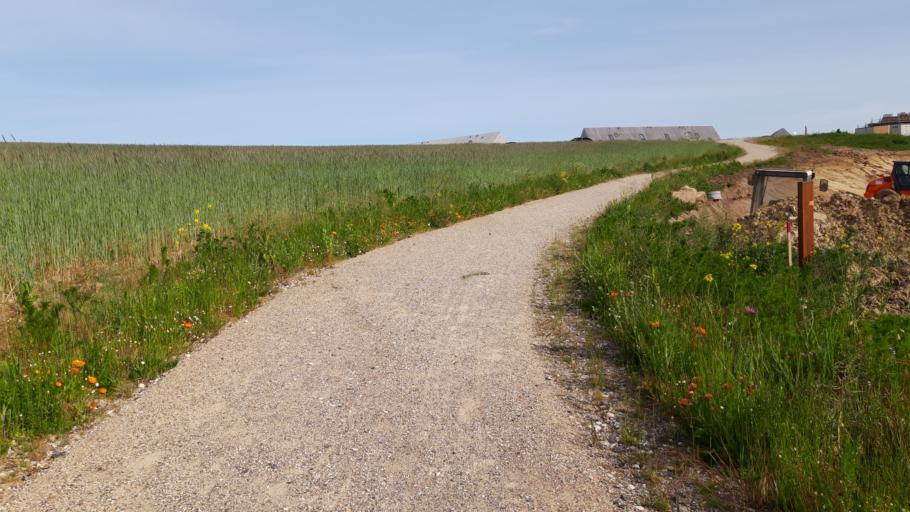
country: DK
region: Central Jutland
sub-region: Arhus Kommune
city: Lystrup
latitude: 56.2325
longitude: 10.2033
